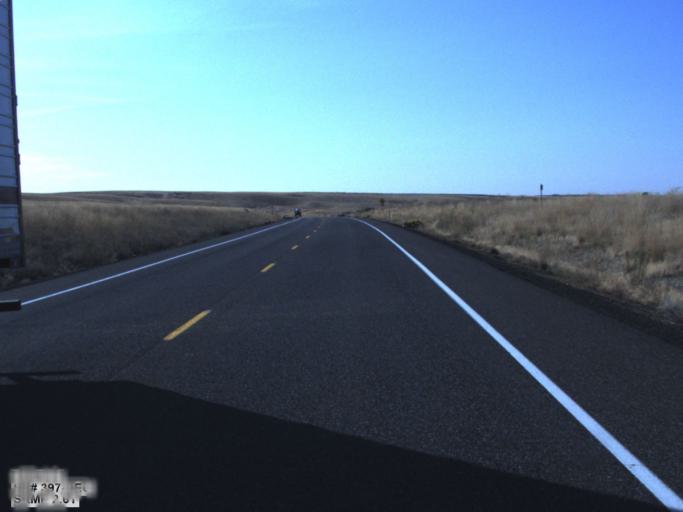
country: US
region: Washington
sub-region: Benton County
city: Highland
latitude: 46.1545
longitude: -119.1532
